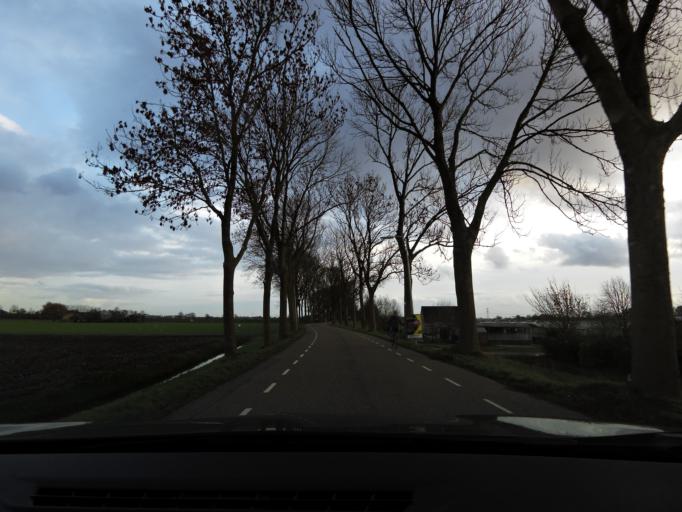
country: NL
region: South Holland
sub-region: Gemeente Binnenmaas
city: Heinenoord
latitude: 51.8236
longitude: 4.4885
